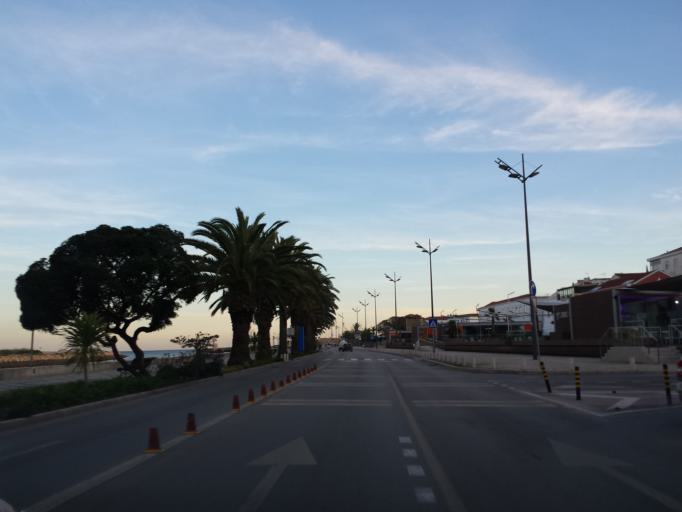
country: PT
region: Faro
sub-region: Lagos
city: Lagos
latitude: 37.1025
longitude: -8.6715
